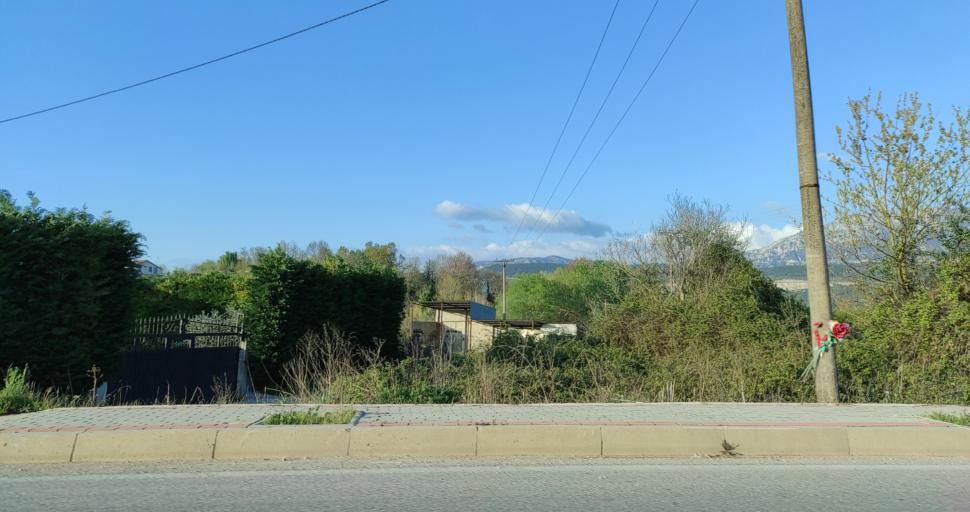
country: AL
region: Durres
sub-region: Rrethi i Krujes
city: Fushe-Kruje
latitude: 41.4906
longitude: 19.7237
